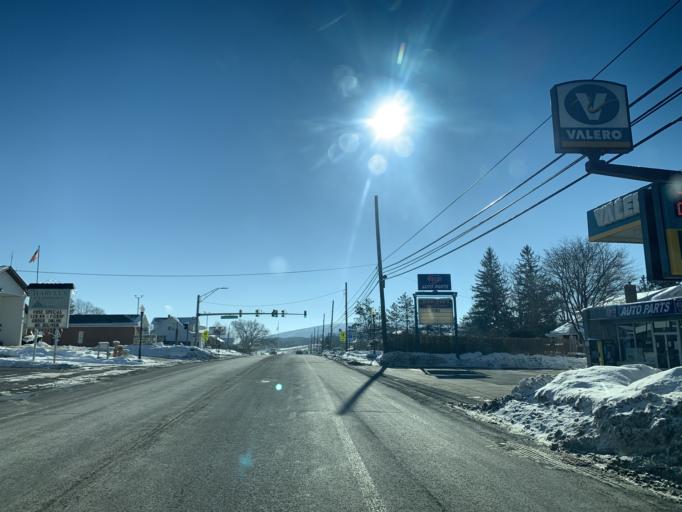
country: US
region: Maryland
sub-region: Allegany County
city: Frostburg
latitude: 39.6523
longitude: -78.9162
